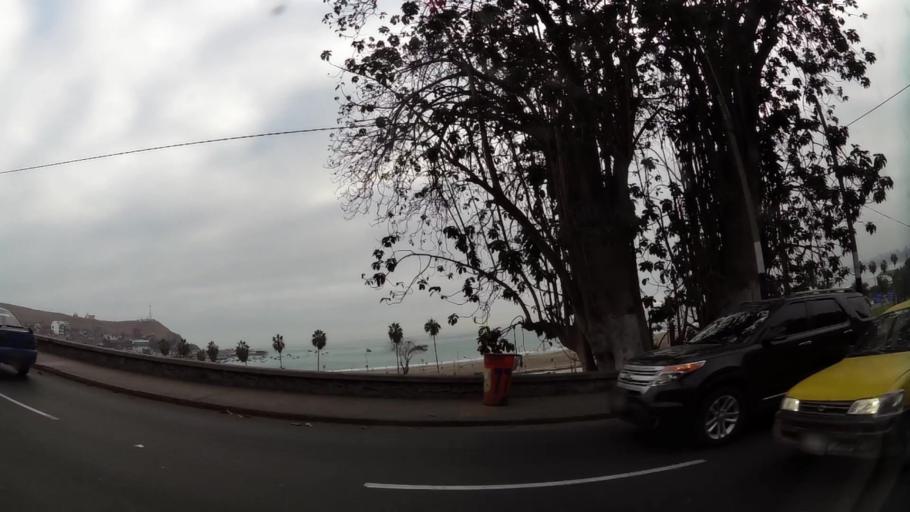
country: PE
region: Lima
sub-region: Lima
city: Surco
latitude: -12.1622
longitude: -77.0249
